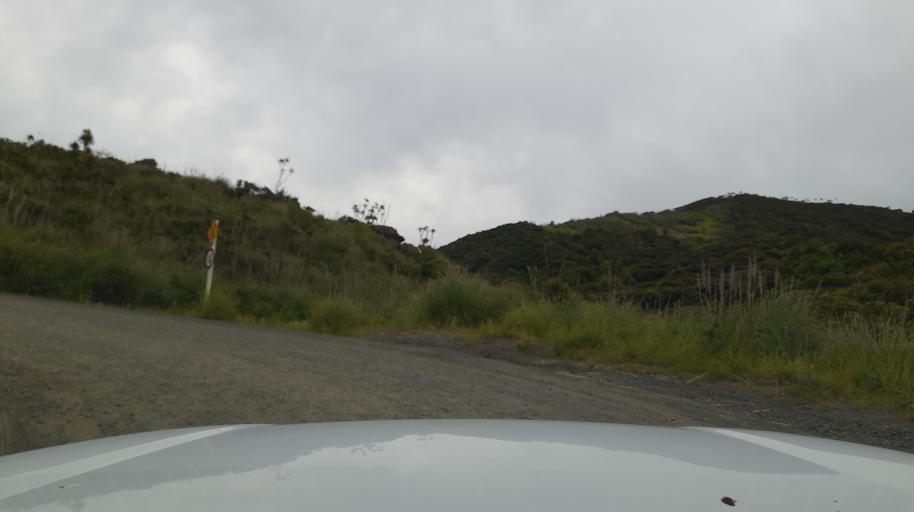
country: NZ
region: Northland
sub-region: Far North District
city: Ahipara
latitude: -35.1800
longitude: 173.1204
